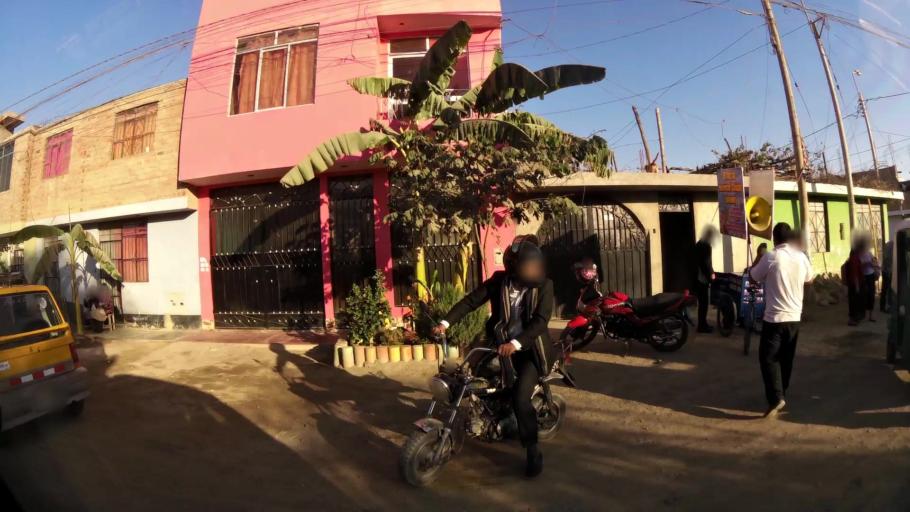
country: PE
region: Ica
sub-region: Provincia de Ica
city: Ica
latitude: -14.0571
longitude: -75.7283
